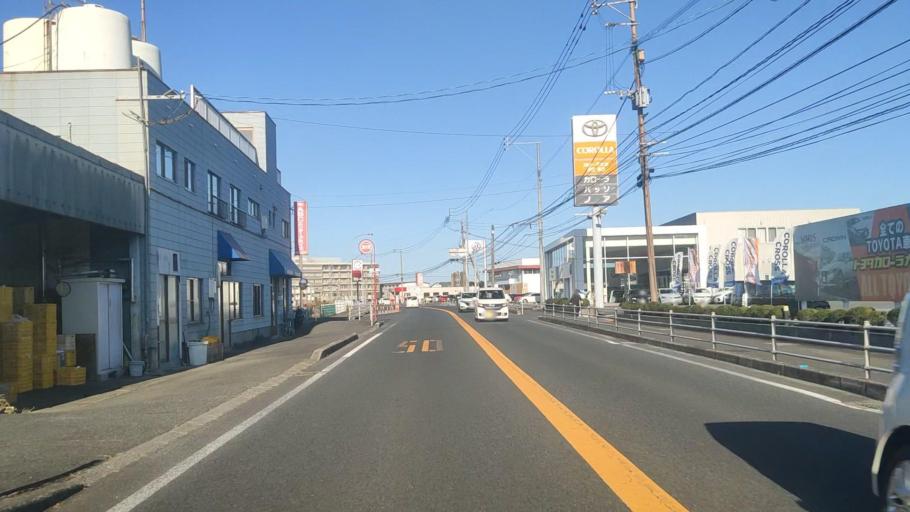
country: JP
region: Oita
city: Oita
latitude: 33.2208
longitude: 131.6169
